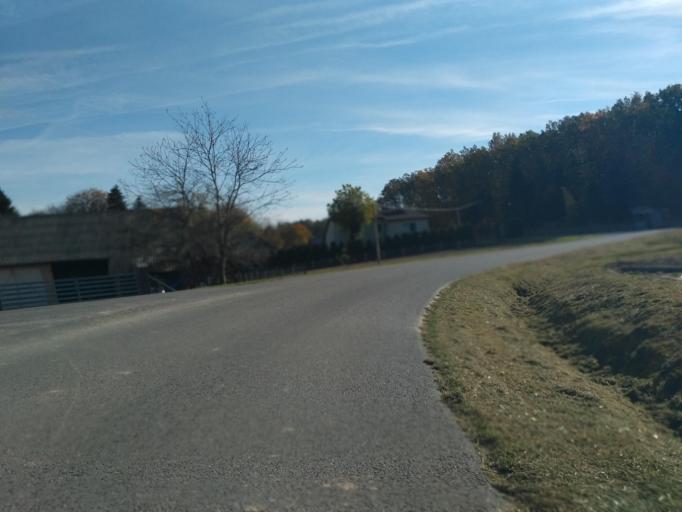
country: PL
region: Subcarpathian Voivodeship
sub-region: Powiat ropczycko-sedziszowski
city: Zagorzyce
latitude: 49.9971
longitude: 21.7165
